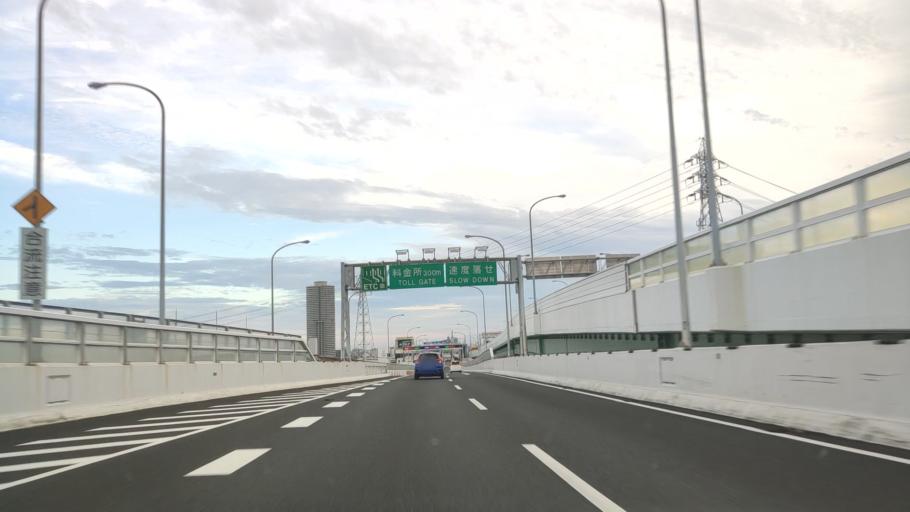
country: JP
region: Aichi
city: Nagoya-shi
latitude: 35.2284
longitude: 136.9100
